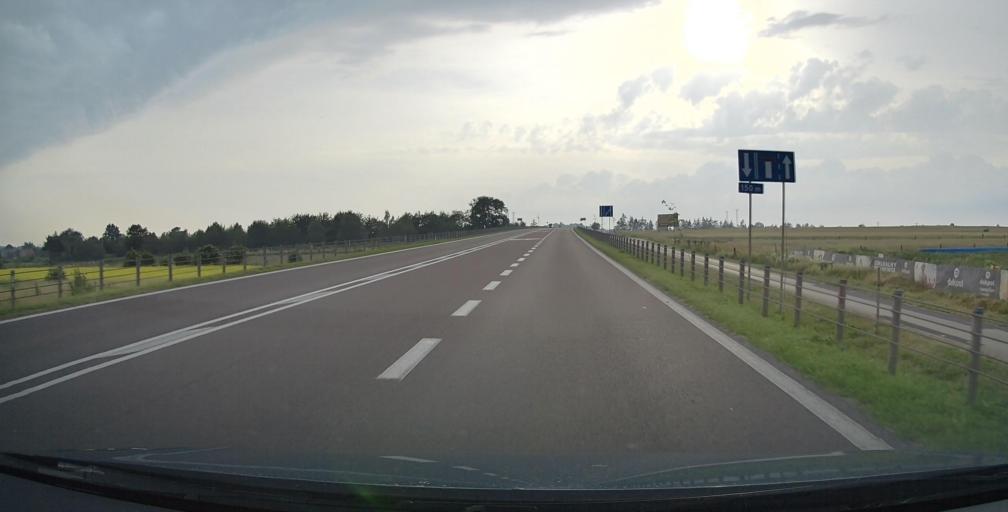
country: PL
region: Masovian Voivodeship
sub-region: Siedlce
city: Siedlce
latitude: 52.1316
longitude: 22.3137
